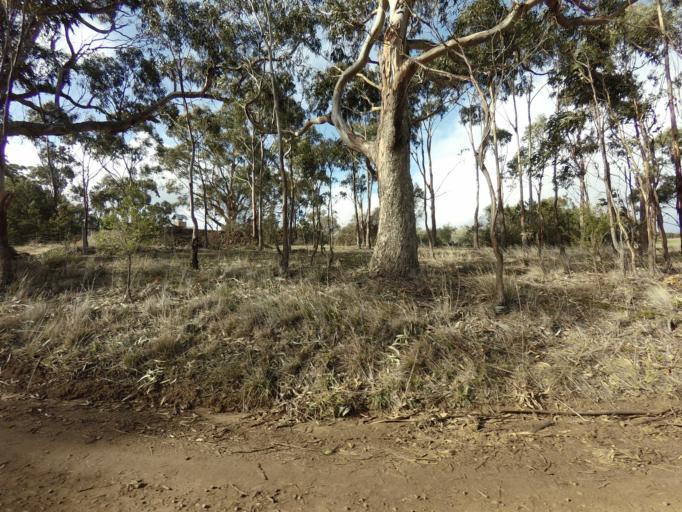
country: AU
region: Tasmania
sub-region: Sorell
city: Sorell
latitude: -42.3086
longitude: 147.9963
